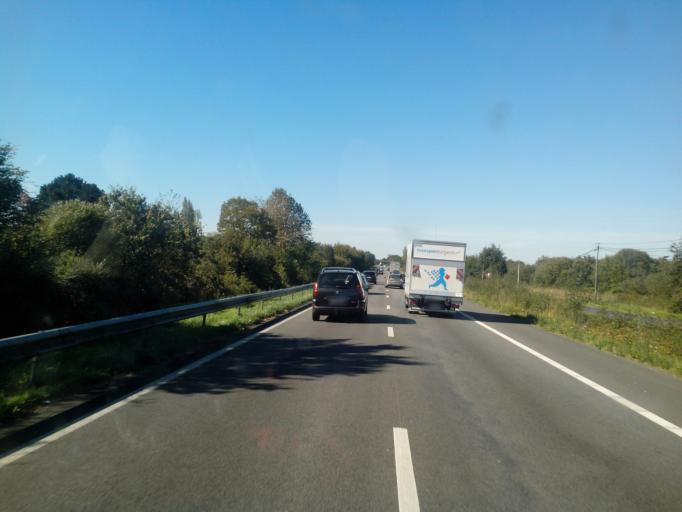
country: FR
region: Pays de la Loire
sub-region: Departement de la Loire-Atlantique
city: Vigneux-de-Bretagne
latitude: 47.2952
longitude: -1.7471
